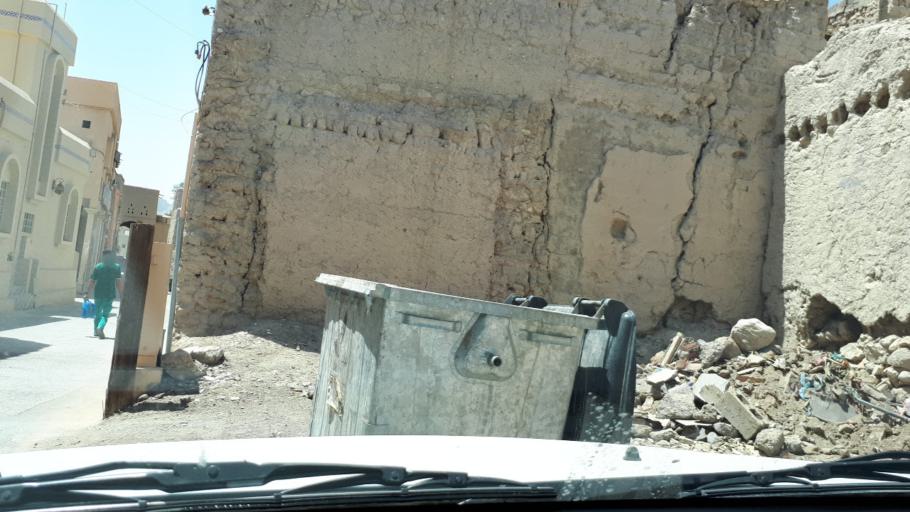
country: OM
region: Muhafazat ad Dakhiliyah
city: Nizwa
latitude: 22.9307
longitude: 57.5316
